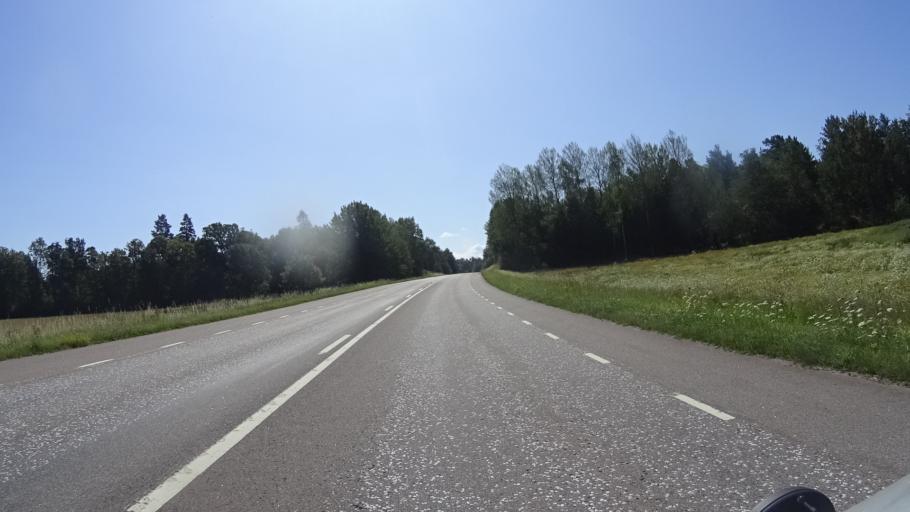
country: SE
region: OEstergoetland
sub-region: Vadstena Kommun
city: Herrestad
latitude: 58.3093
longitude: 14.9093
